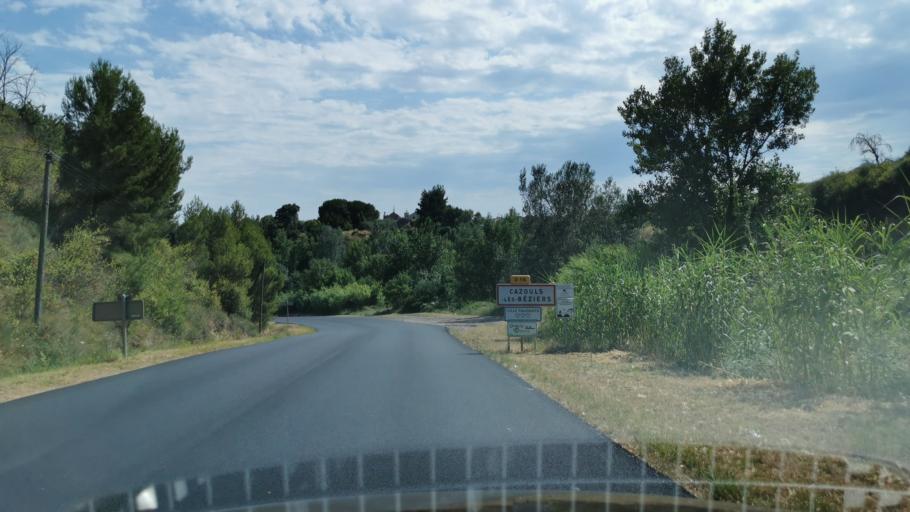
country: FR
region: Languedoc-Roussillon
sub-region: Departement de l'Herault
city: Cazouls-les-Beziers
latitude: 43.3984
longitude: 3.1032
